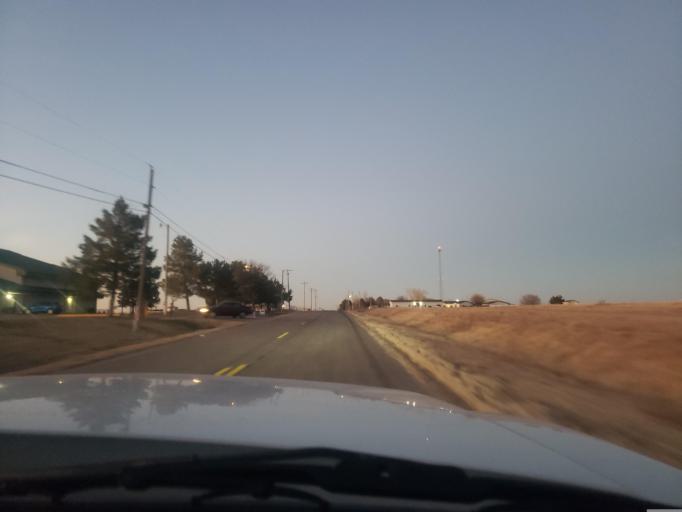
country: US
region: Kansas
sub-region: Finney County
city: Garden City
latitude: 37.9942
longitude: -100.8749
